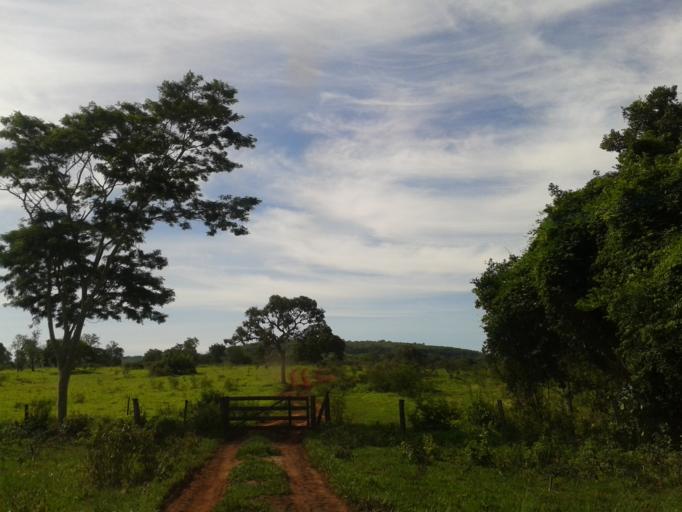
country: BR
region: Minas Gerais
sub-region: Santa Vitoria
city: Santa Vitoria
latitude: -19.0905
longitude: -50.0160
